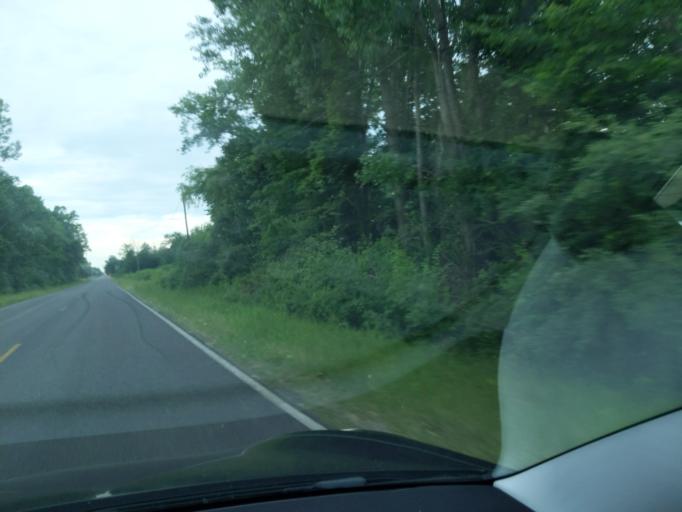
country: US
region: Michigan
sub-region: Isabella County
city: Mount Pleasant
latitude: 43.6177
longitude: -84.7279
